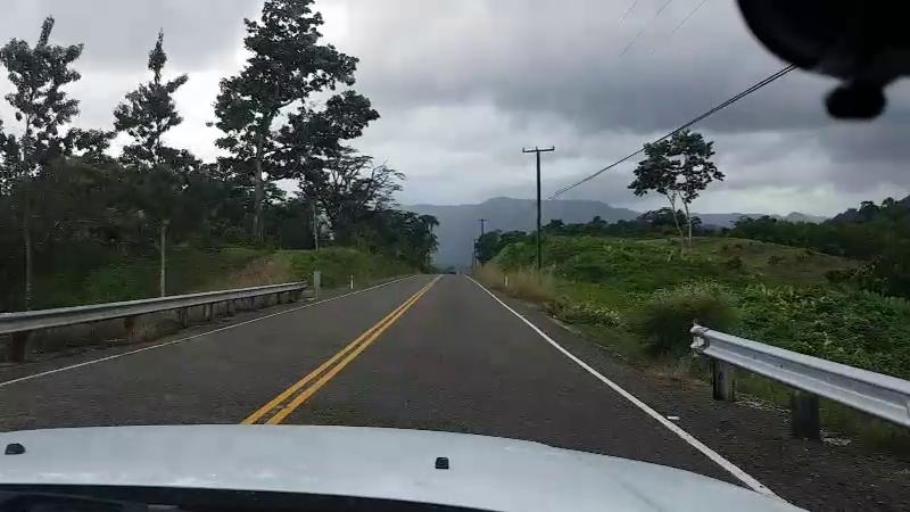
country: BZ
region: Cayo
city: Belmopan
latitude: 17.1142
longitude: -88.6572
